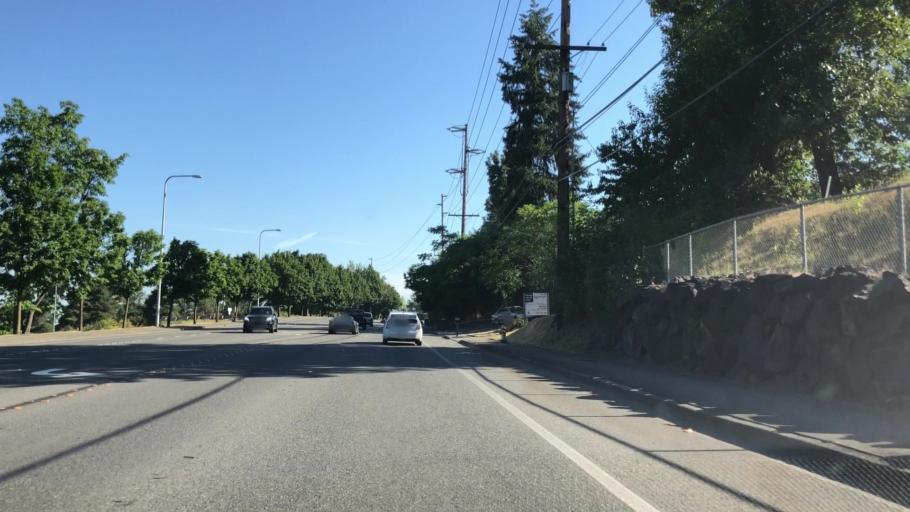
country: US
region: Washington
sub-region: King County
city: Newport
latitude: 47.5654
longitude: -122.1705
